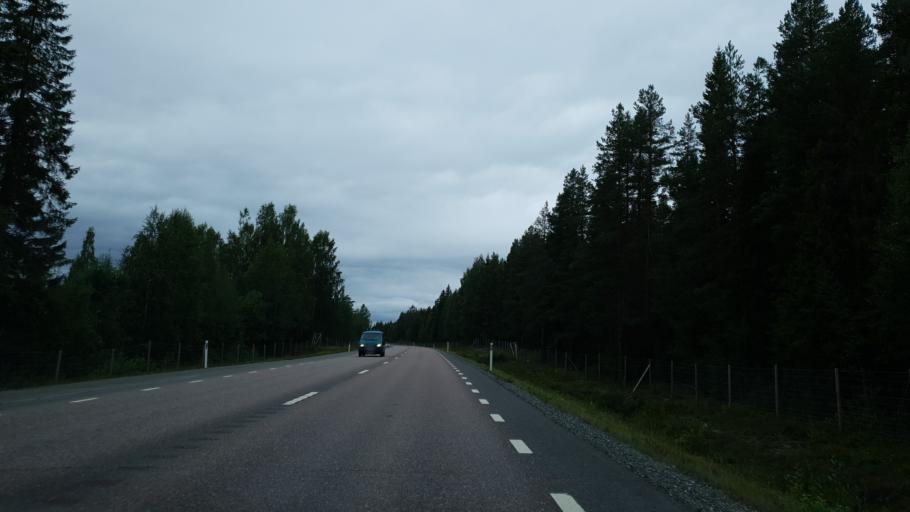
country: SE
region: Vaesterbotten
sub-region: Skelleftea Kommun
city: Viken
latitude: 64.7800
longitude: 20.8222
